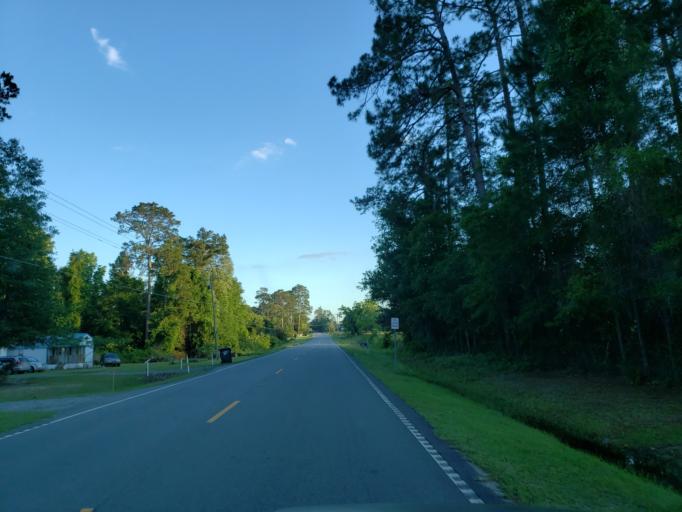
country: US
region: Georgia
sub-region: Lowndes County
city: Valdosta
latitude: 30.7427
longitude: -83.2518
